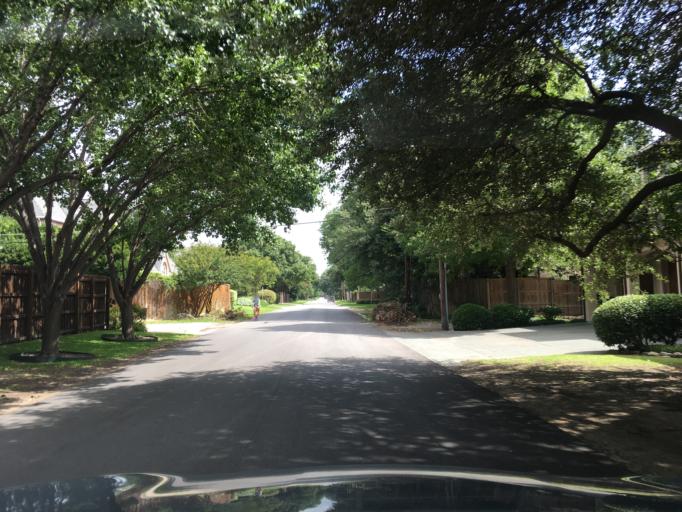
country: US
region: Texas
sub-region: Dallas County
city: University Park
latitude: 32.8864
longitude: -96.7900
